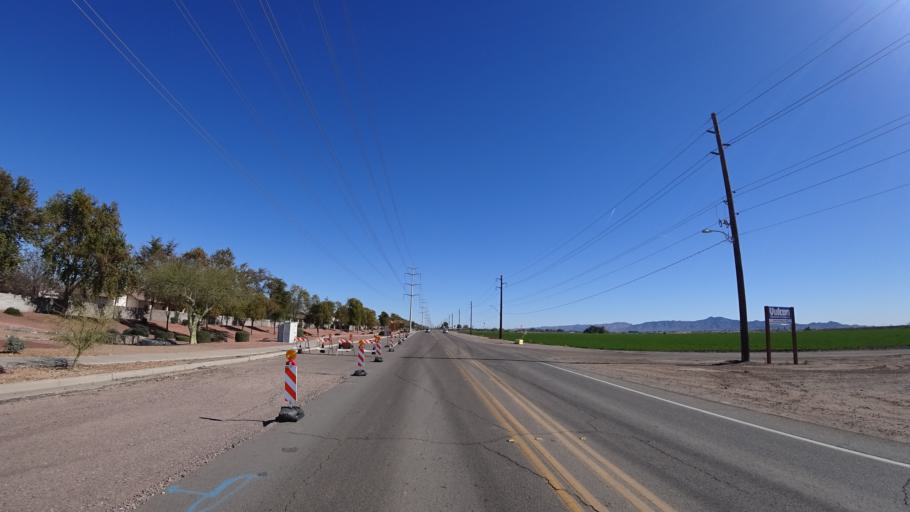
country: US
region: Arizona
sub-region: Maricopa County
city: Tolleson
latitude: 33.4084
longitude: -112.2297
